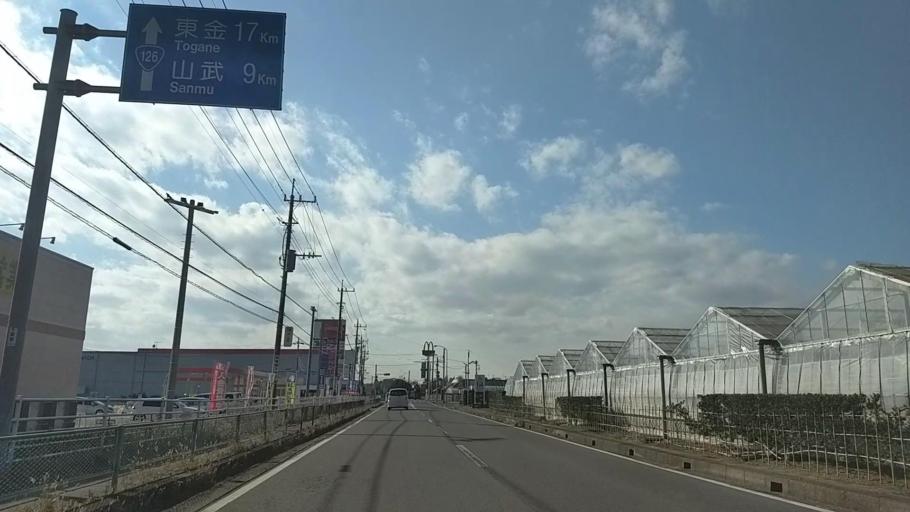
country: JP
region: Chiba
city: Yokaichiba
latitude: 35.6611
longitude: 140.4858
